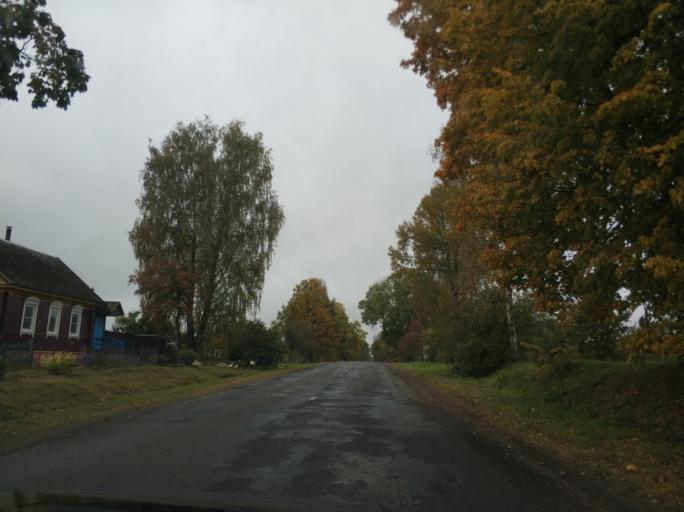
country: BY
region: Vitebsk
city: Polatsk
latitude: 55.4299
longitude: 28.9991
